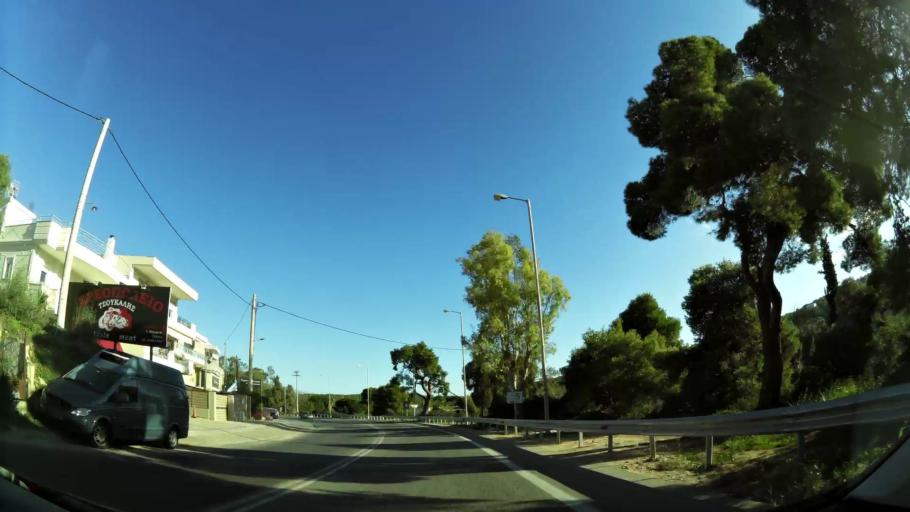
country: GR
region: Attica
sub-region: Nomarchia Anatolikis Attikis
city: Rafina
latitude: 38.0190
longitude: 23.9951
